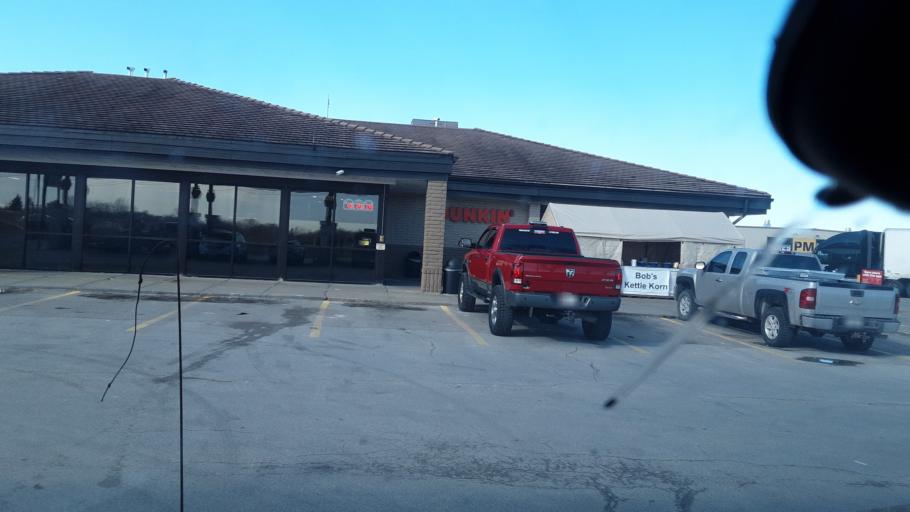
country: US
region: Missouri
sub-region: Warren County
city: Warrenton
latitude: 38.8399
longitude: -91.2276
